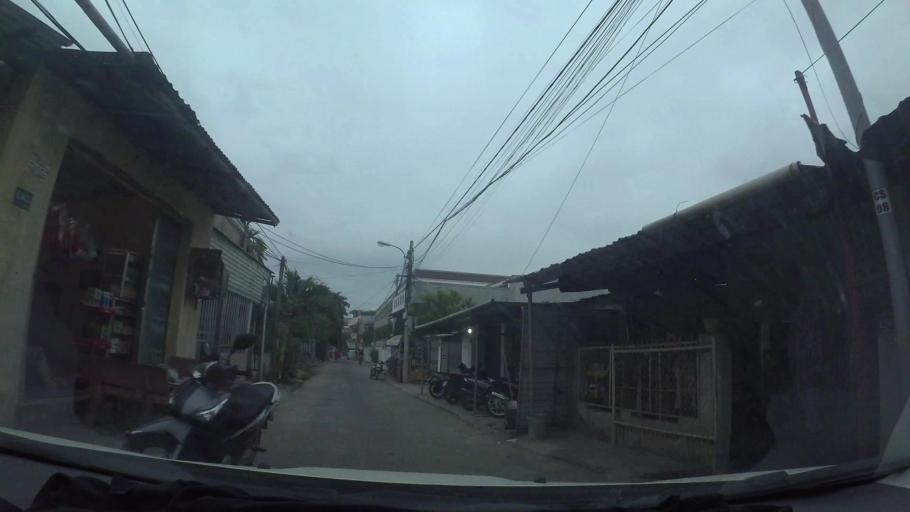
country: VN
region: Da Nang
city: Lien Chieu
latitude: 16.0850
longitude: 108.1532
